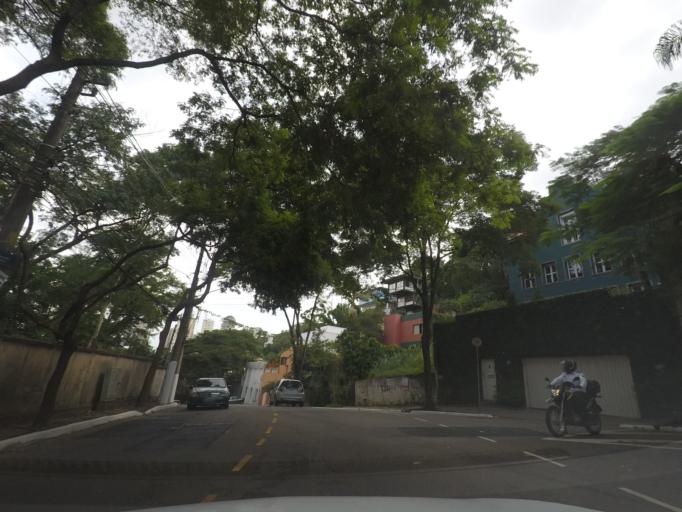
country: BR
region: Sao Paulo
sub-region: Taboao Da Serra
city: Taboao da Serra
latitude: -23.6222
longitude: -46.7158
